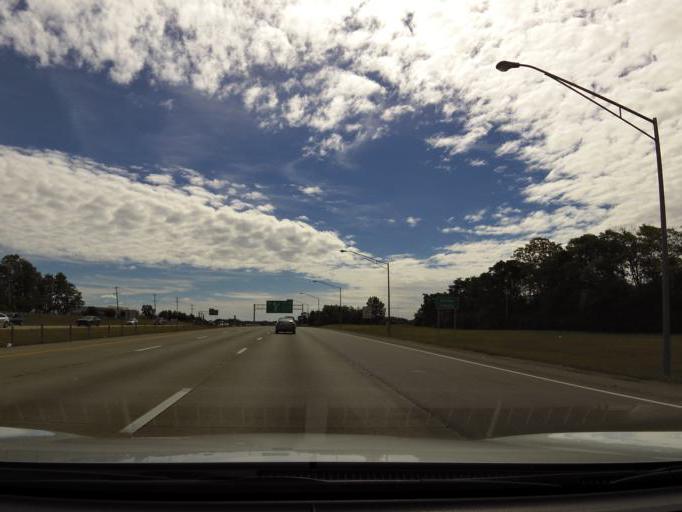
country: US
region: Kentucky
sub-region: Kenton County
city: Villa Hills
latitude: 39.0503
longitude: -84.6211
